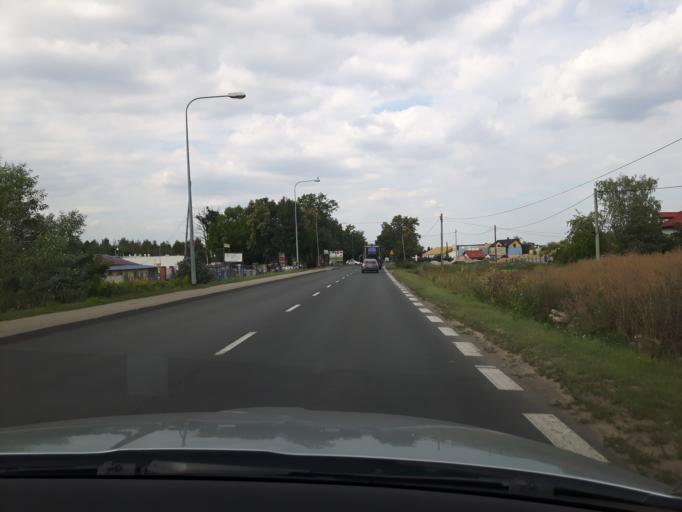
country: PL
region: Masovian Voivodeship
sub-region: Powiat legionowski
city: Stanislawow Pierwszy
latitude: 52.3415
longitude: 21.0287
